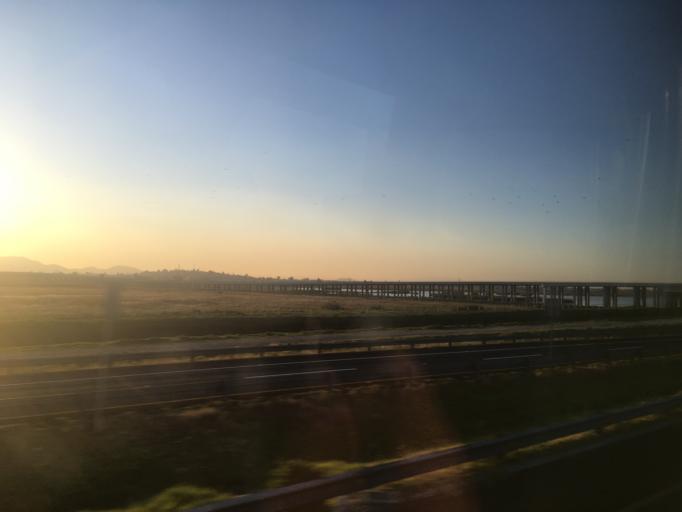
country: MX
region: Mexico
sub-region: Lerma
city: Colonia Isidro Fabela
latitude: 19.3201
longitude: -99.5214
